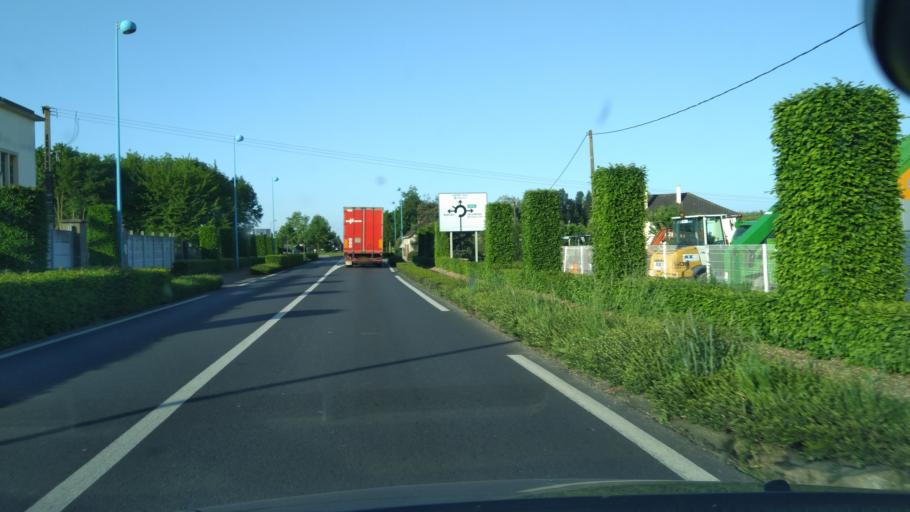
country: FR
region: Pays de la Loire
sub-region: Departement de la Mayenne
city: Craon
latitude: 47.8441
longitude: -0.9665
